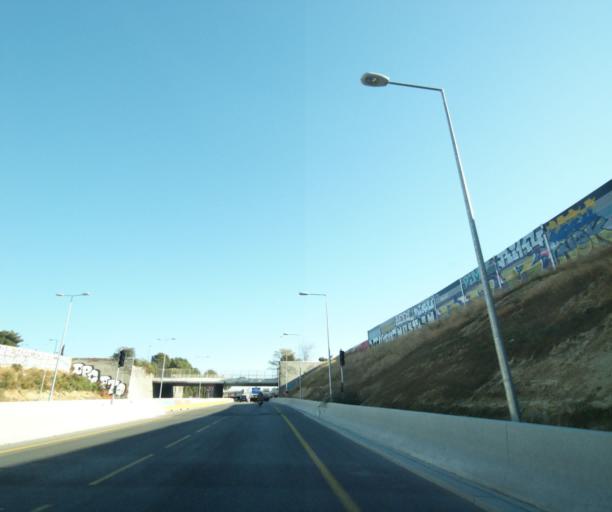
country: FR
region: Provence-Alpes-Cote d'Azur
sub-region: Departement des Bouches-du-Rhone
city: Marseille 13
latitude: 43.3295
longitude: 5.4123
